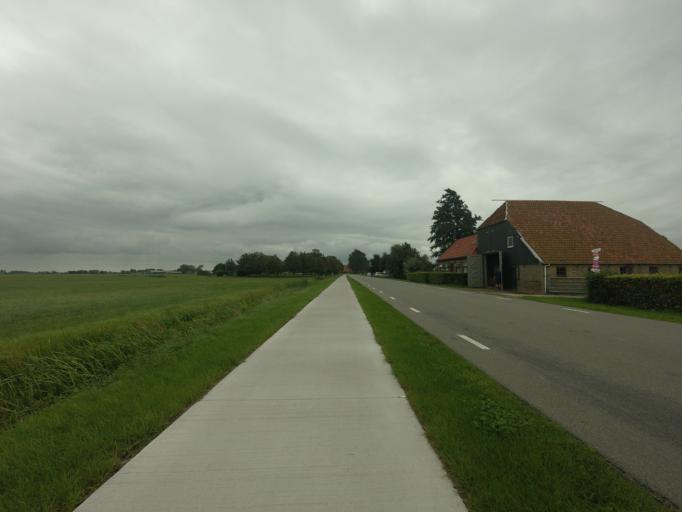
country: NL
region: Friesland
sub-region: Sudwest Fryslan
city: Heeg
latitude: 52.9814
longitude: 5.5962
